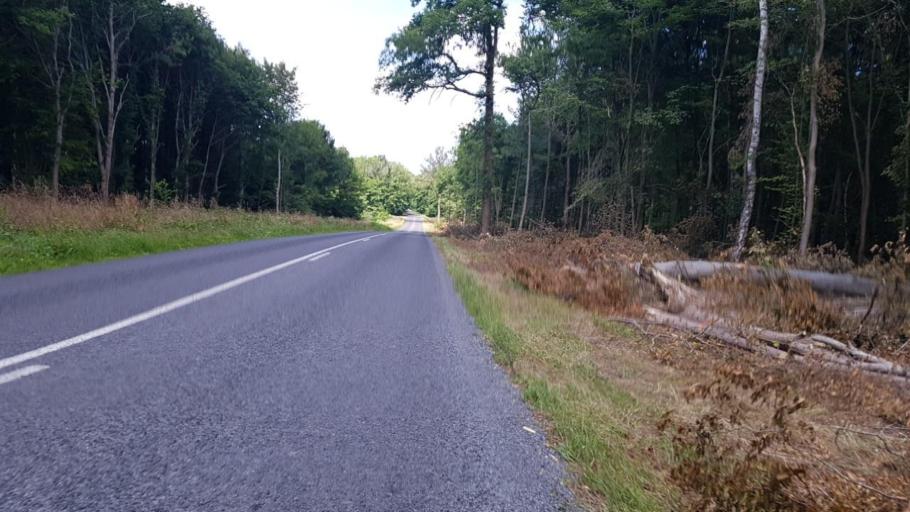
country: FR
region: Picardie
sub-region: Departement de l'Oise
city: Chiry-Ourscamp
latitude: 49.5333
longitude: 2.9848
